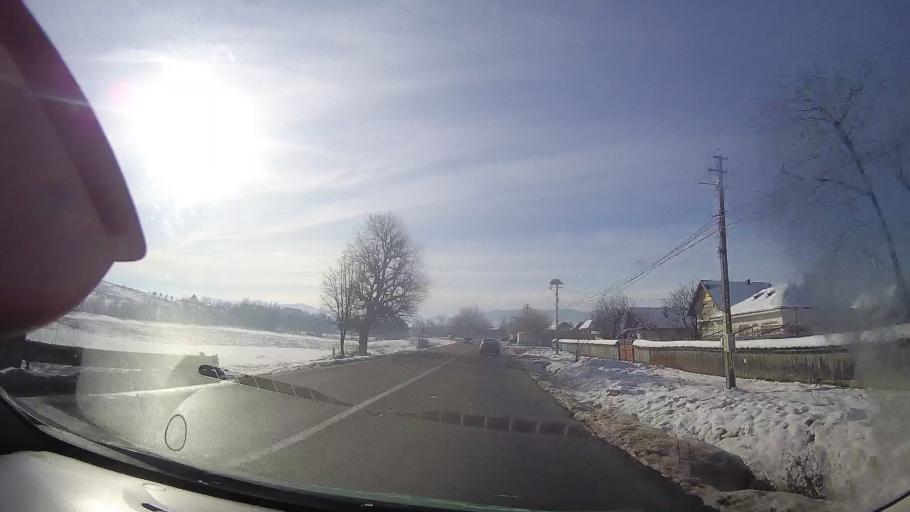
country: RO
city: Vanatori-Neamt
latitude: 47.1843
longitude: 26.3336
